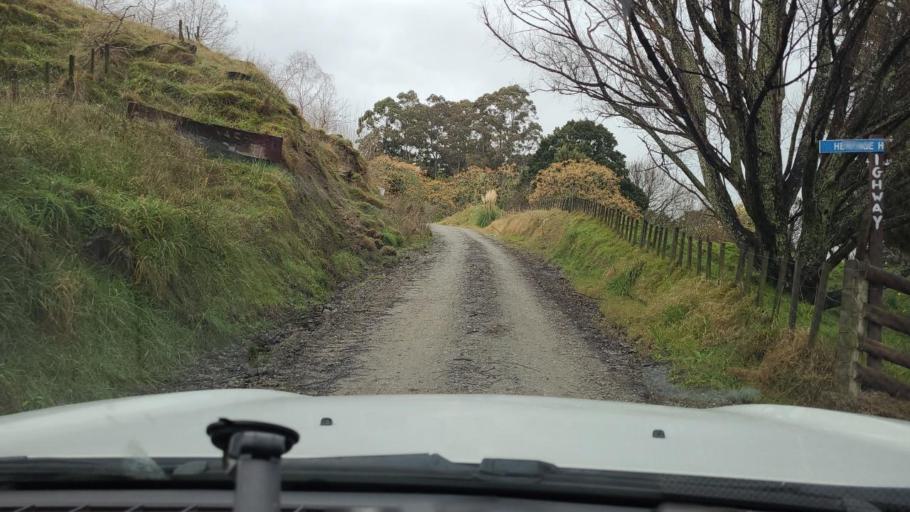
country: NZ
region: Gisborne
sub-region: Gisborne District
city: Gisborne
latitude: -38.5660
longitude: 177.7941
